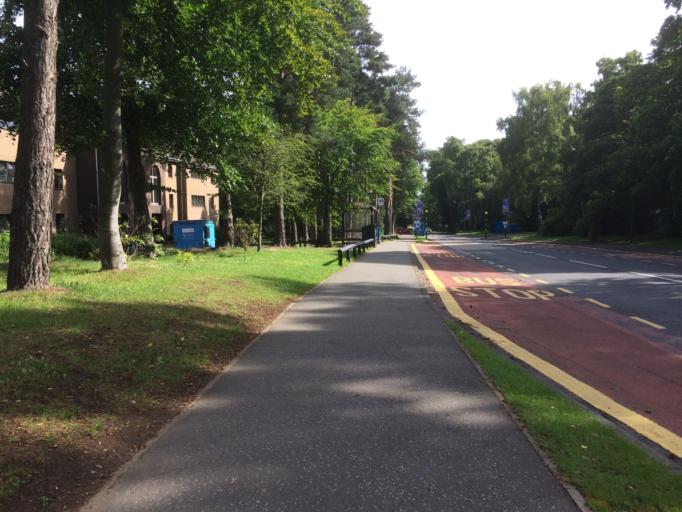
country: GB
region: Scotland
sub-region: Edinburgh
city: Currie
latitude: 55.9101
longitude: -3.3180
